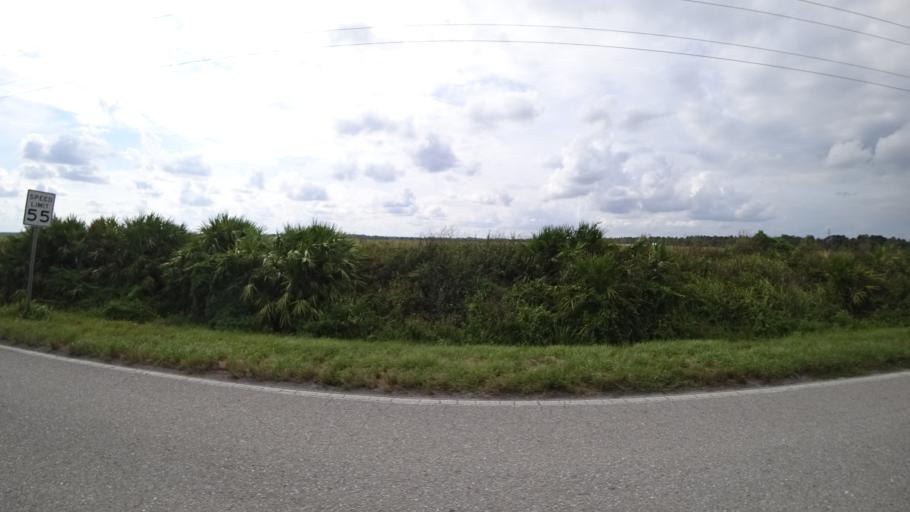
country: US
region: Florida
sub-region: Hillsborough County
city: Wimauma
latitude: 27.5863
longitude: -82.1038
